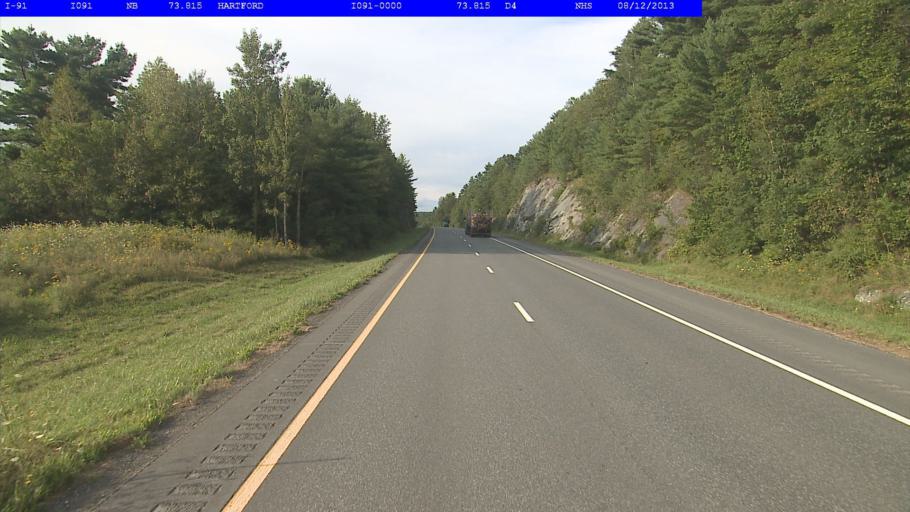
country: US
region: Vermont
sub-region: Windsor County
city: Wilder
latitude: 43.6916
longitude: -72.3111
